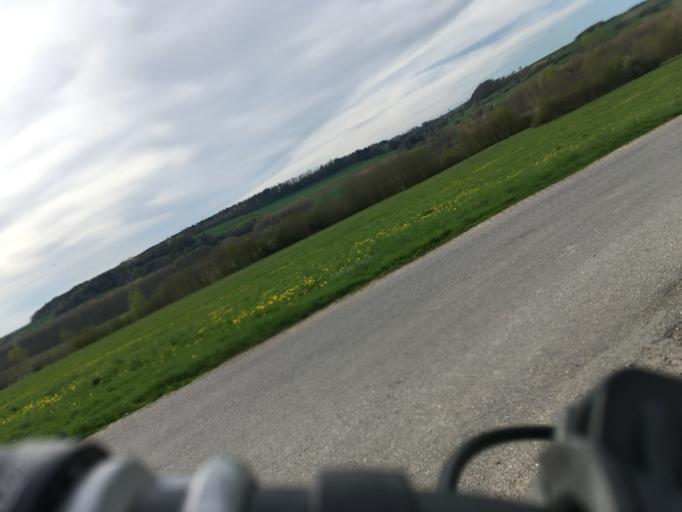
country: CH
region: Schaffhausen
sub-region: Bezirk Reiat
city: Thayngen
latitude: 47.7979
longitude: 8.7278
